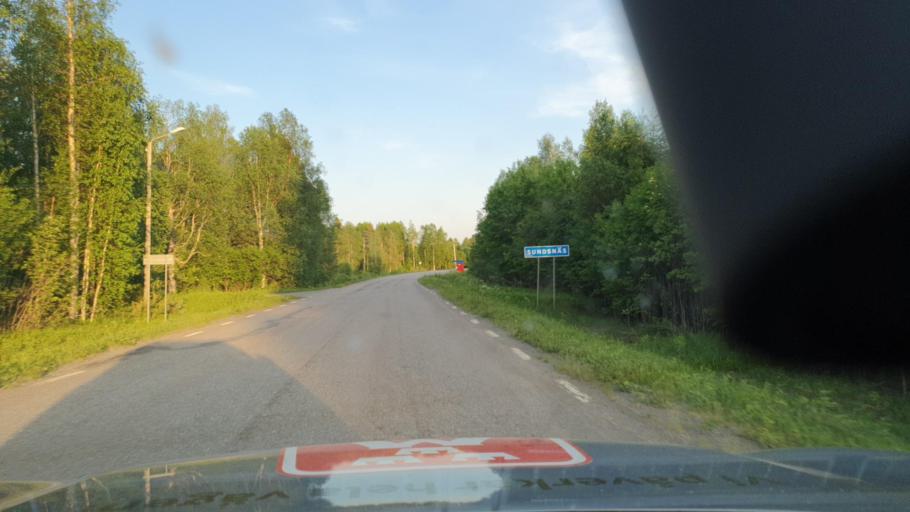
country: SE
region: Norrbotten
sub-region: Bodens Kommun
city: Boden
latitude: 66.0410
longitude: 21.8028
